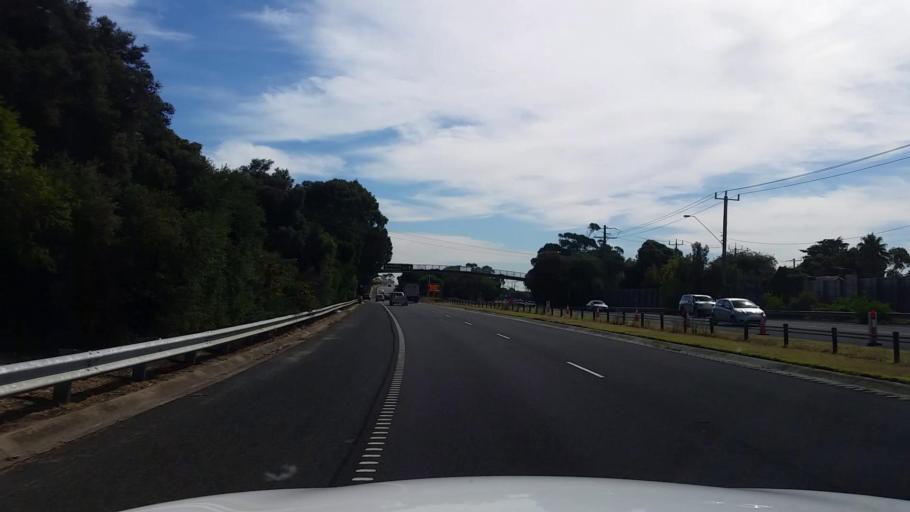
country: AU
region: Victoria
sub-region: Frankston
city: Frankston East
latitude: -38.1330
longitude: 145.1361
